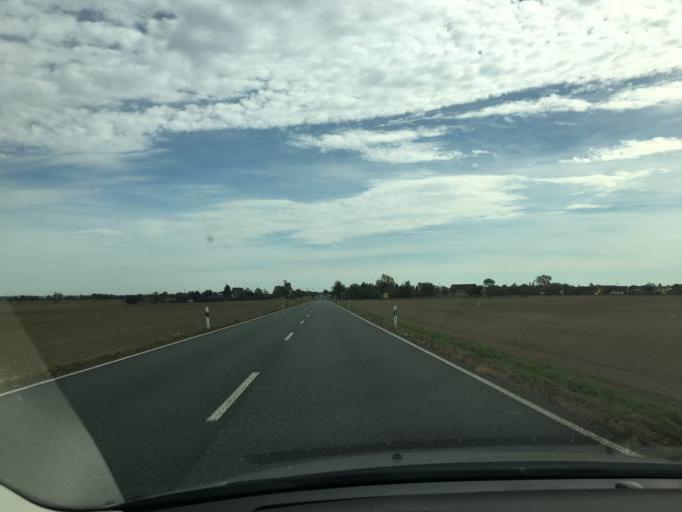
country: DE
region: Saxony
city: Riesa
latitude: 51.2551
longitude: 13.2795
